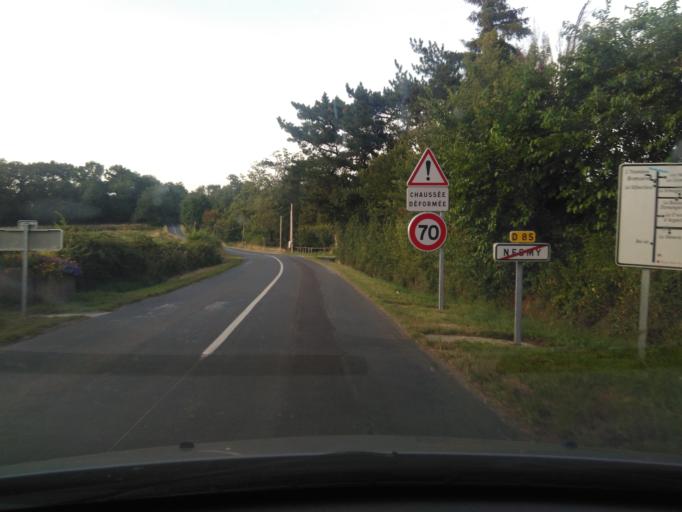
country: FR
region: Pays de la Loire
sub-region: Departement de la Vendee
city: Nesmy
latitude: 46.5949
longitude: -1.4054
